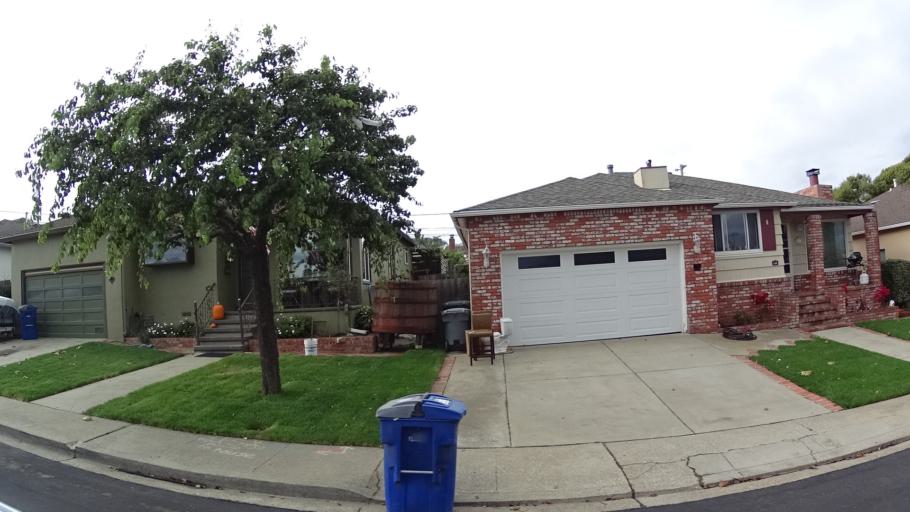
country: US
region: California
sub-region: San Mateo County
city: San Bruno
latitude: 37.6376
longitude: -122.4308
